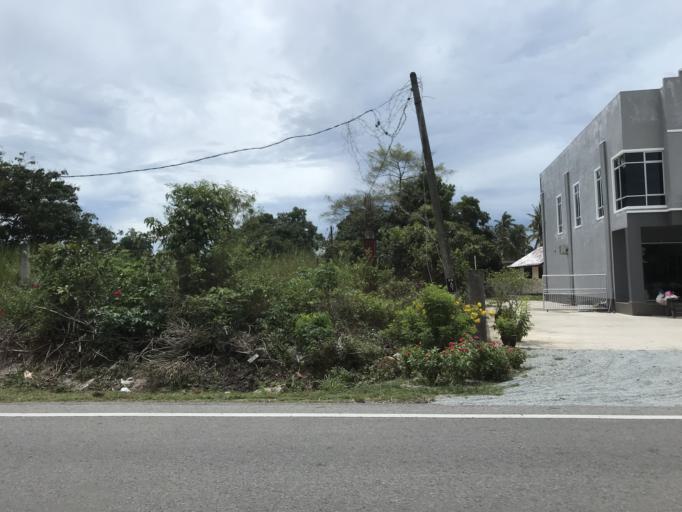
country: MY
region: Kelantan
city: Tumpat
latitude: 6.1761
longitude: 102.1950
